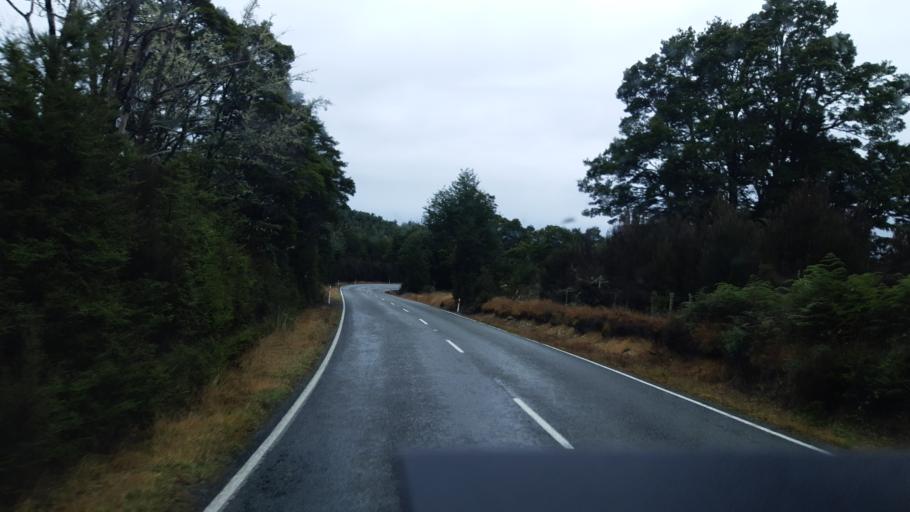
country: NZ
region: Tasman
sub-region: Tasman District
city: Wakefield
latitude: -41.7759
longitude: 172.8919
